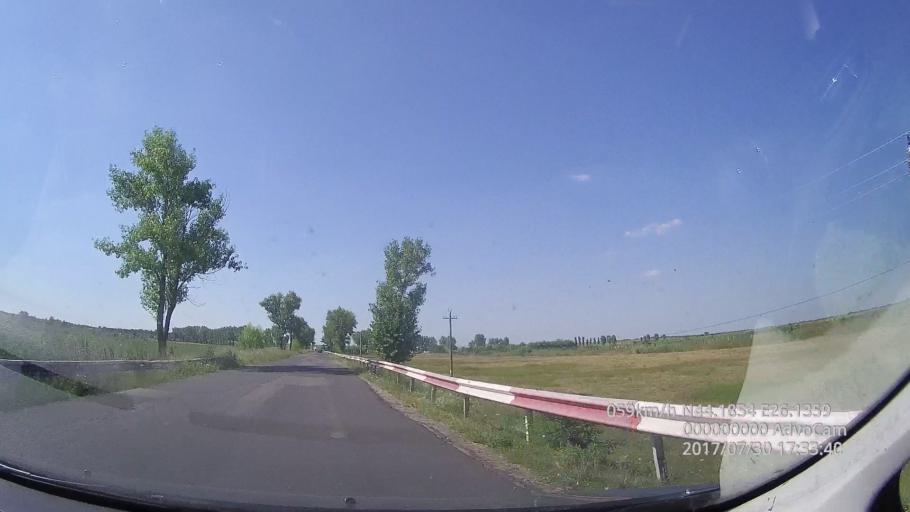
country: RO
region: Giurgiu
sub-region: Comuna Comana
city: Comana
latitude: 44.1860
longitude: 26.1357
